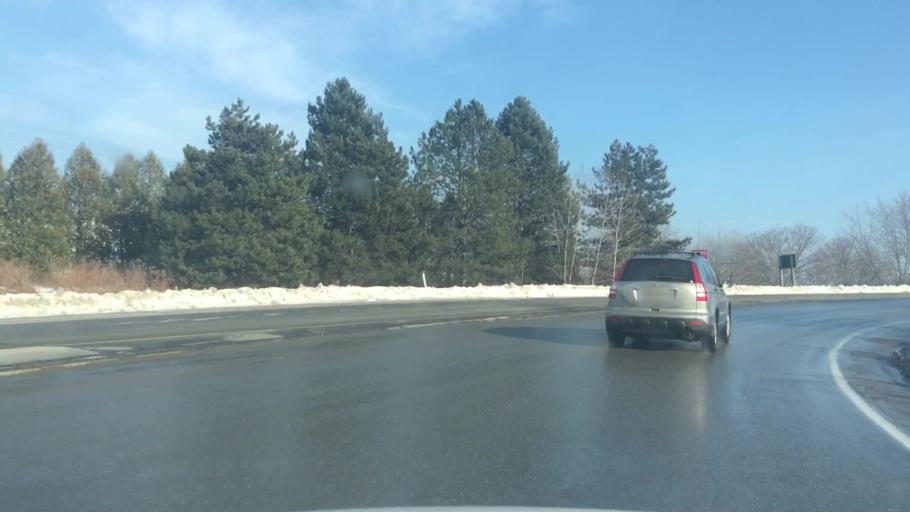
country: US
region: Maine
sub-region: Penobscot County
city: Brewer
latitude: 44.7854
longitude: -68.7706
